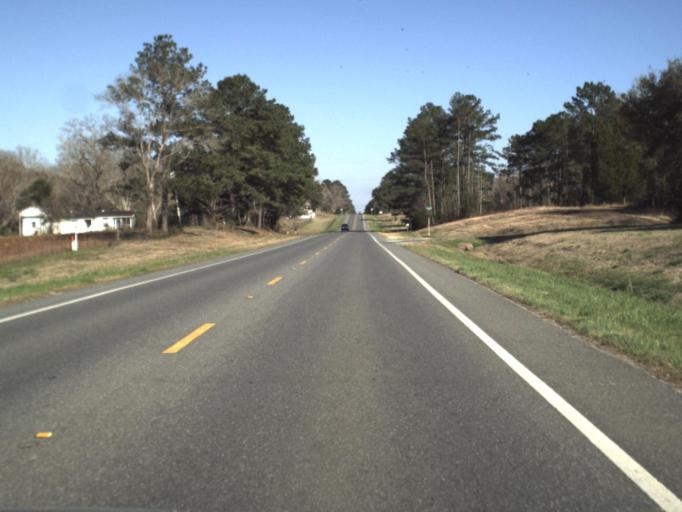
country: US
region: Florida
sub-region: Jackson County
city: Marianna
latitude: 30.7849
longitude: -85.3313
